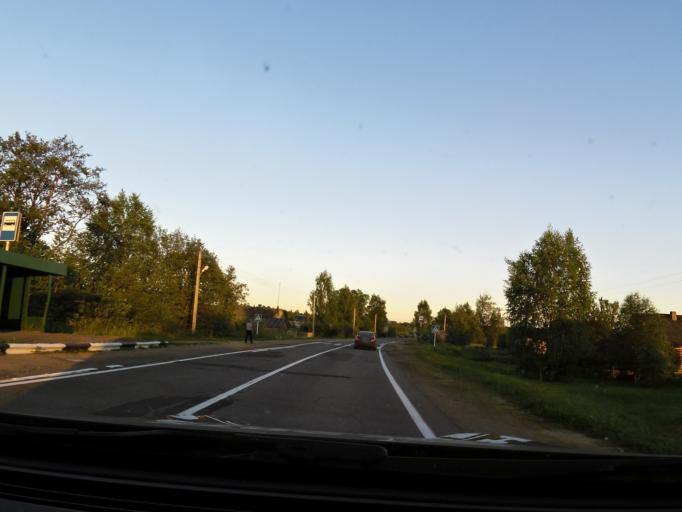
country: RU
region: Jaroslavl
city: Prechistoye
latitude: 58.3759
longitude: 40.4816
